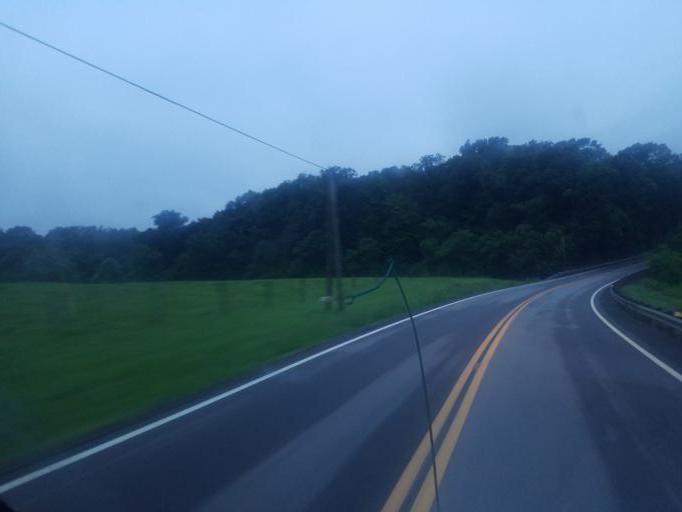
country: US
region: Ohio
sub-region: Carroll County
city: Carrollton
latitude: 40.5065
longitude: -81.0381
